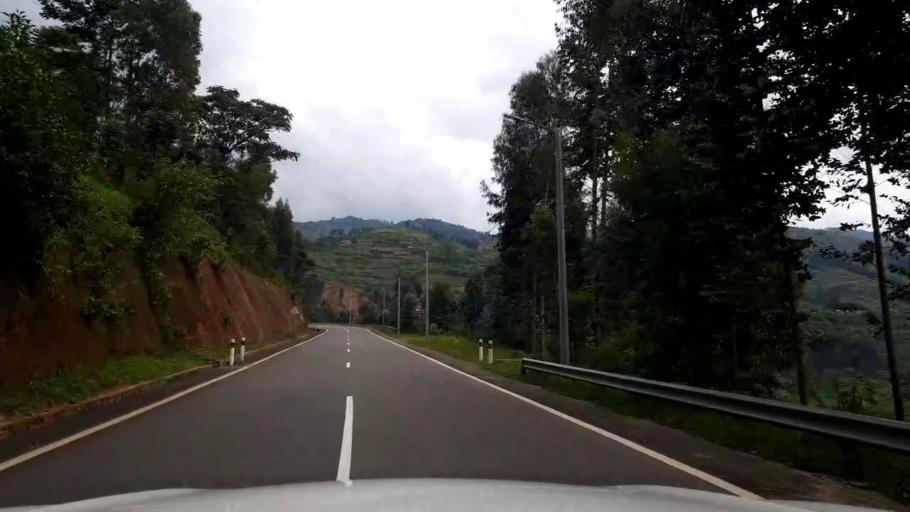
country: RW
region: Western Province
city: Kibuye
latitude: -1.9315
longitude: 29.3730
